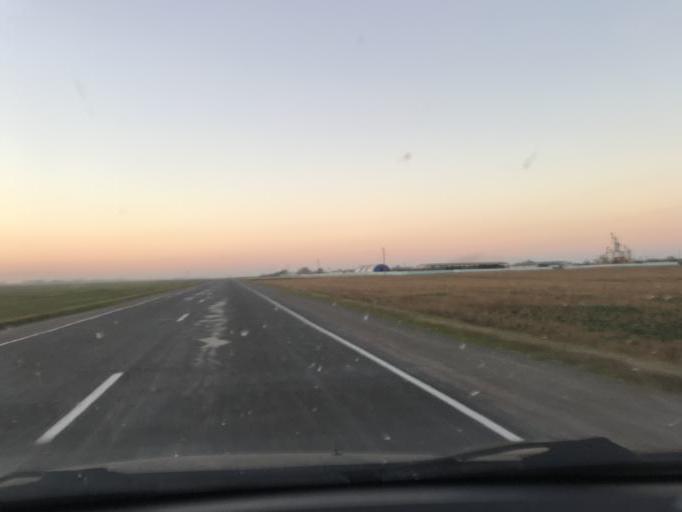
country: BY
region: Gomel
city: Horad Rechytsa
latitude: 52.2431
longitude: 30.5012
